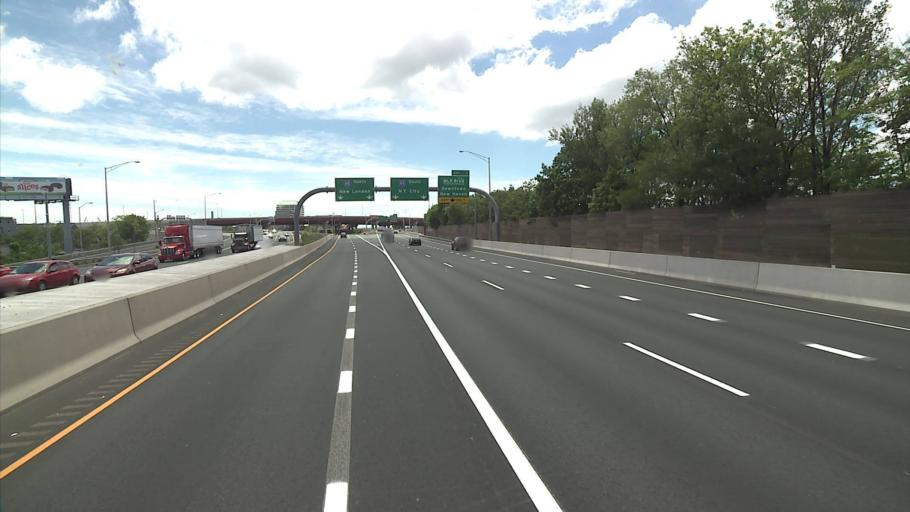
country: US
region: Connecticut
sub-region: New Haven County
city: New Haven
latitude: 41.3052
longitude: -72.9143
